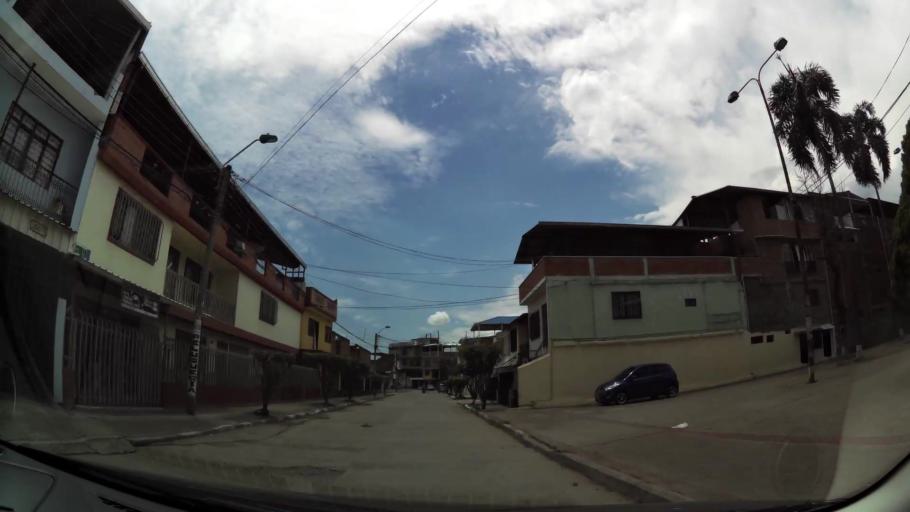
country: CO
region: Valle del Cauca
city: Cali
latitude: 3.4457
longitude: -76.4889
